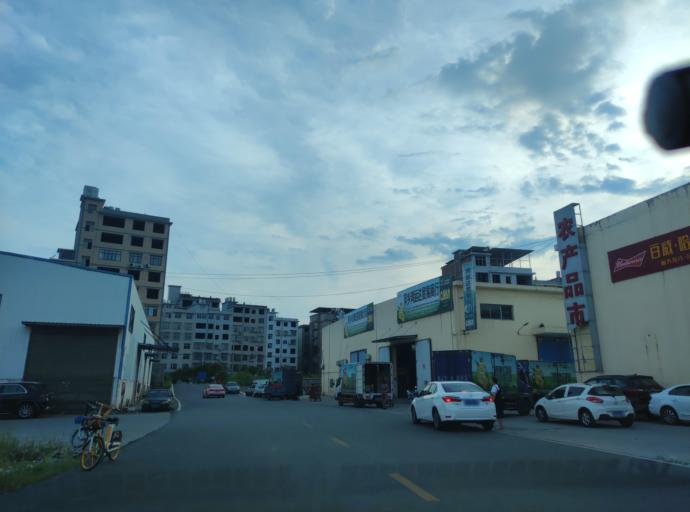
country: CN
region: Jiangxi Sheng
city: Pingxiang
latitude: 27.6417
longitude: 113.8795
